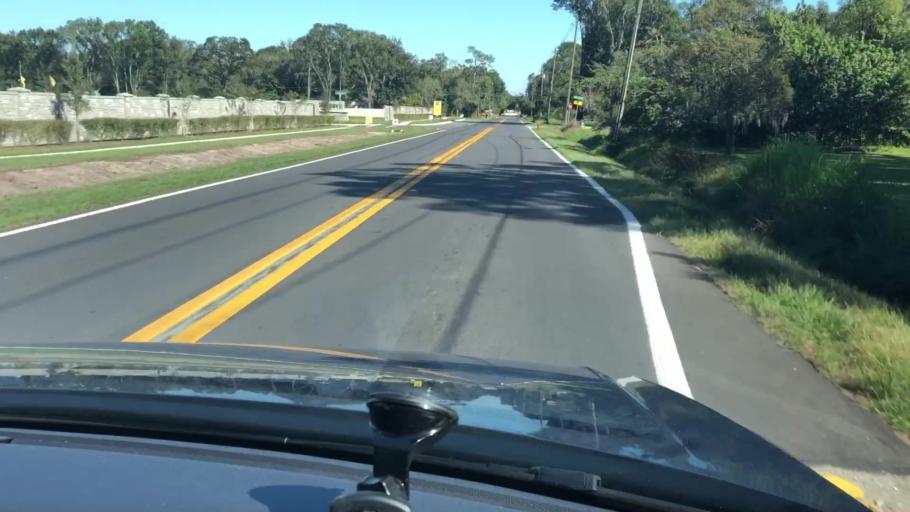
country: US
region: Florida
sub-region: Polk County
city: Gibsonia
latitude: 28.1354
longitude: -81.9818
